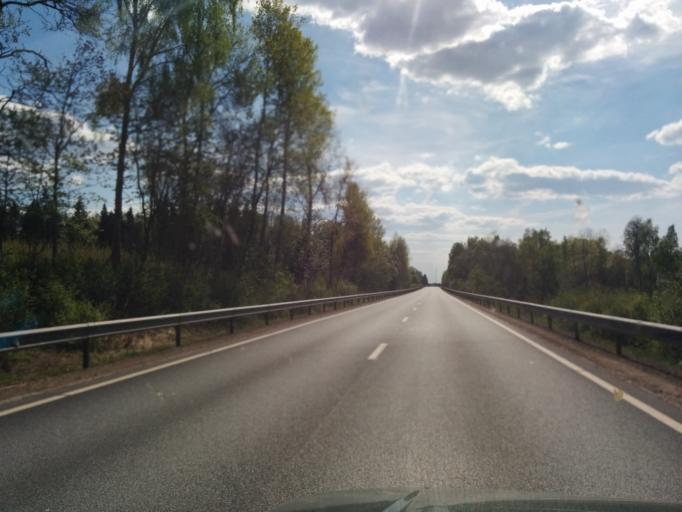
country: LV
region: Sigulda
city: Sigulda
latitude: 57.2337
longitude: 24.8177
